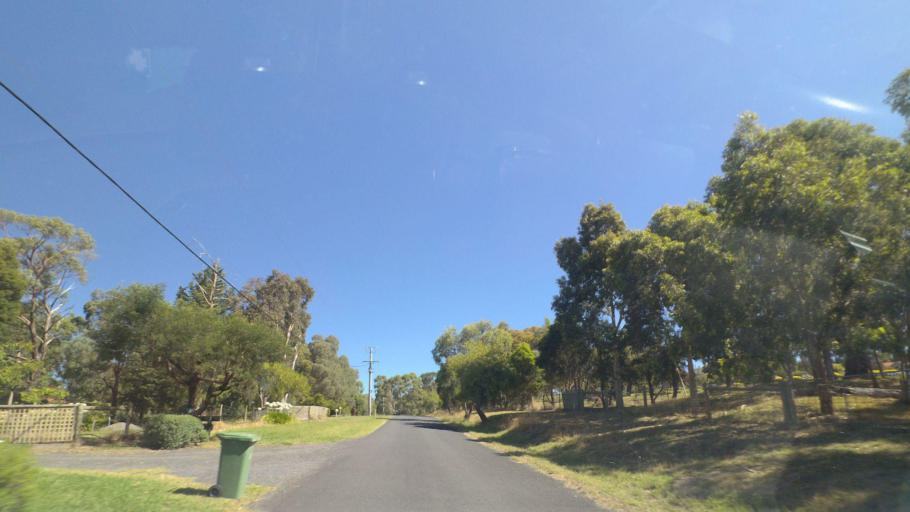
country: AU
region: Victoria
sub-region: Yarra Ranges
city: Chirnside Park
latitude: -37.7389
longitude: 145.3288
